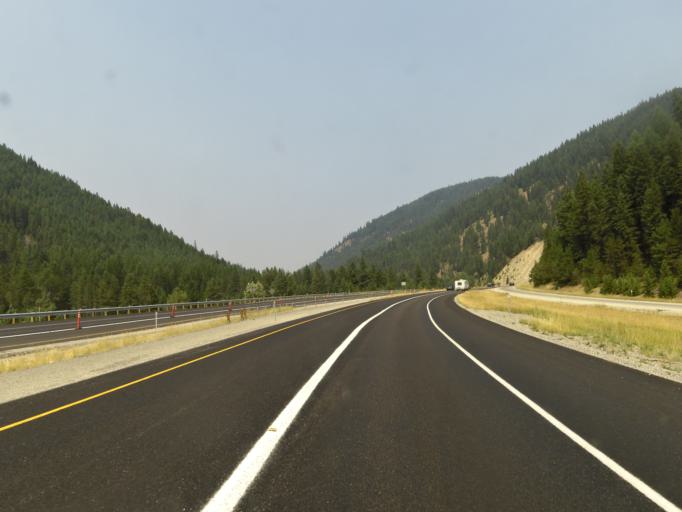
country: US
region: Montana
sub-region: Sanders County
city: Thompson Falls
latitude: 47.3229
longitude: -115.2485
